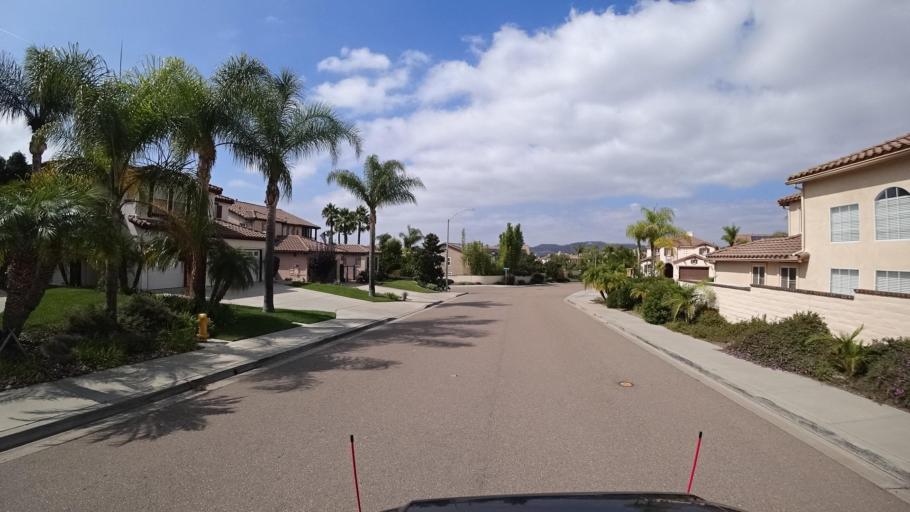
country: US
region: California
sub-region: San Diego County
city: Fairbanks Ranch
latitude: 33.0097
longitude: -117.1083
